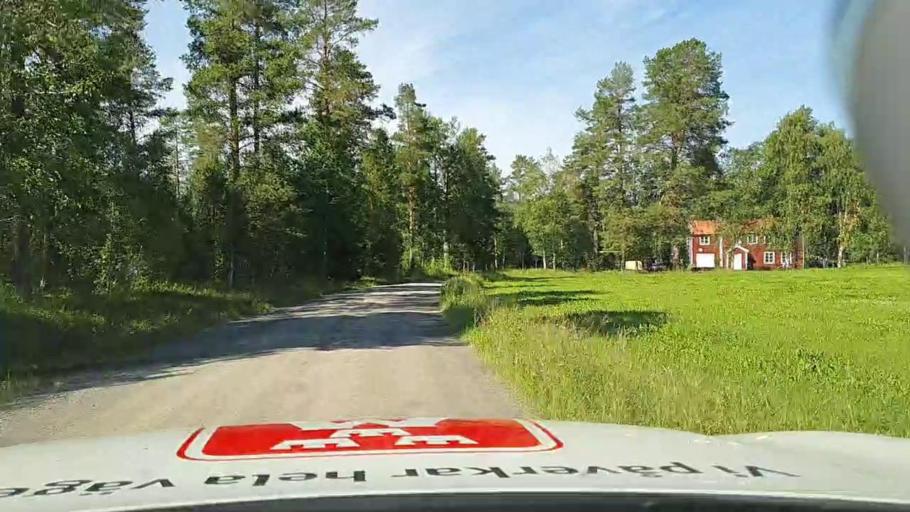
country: SE
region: Jaemtland
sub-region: Stroemsunds Kommun
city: Stroemsund
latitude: 63.6958
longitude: 15.3619
